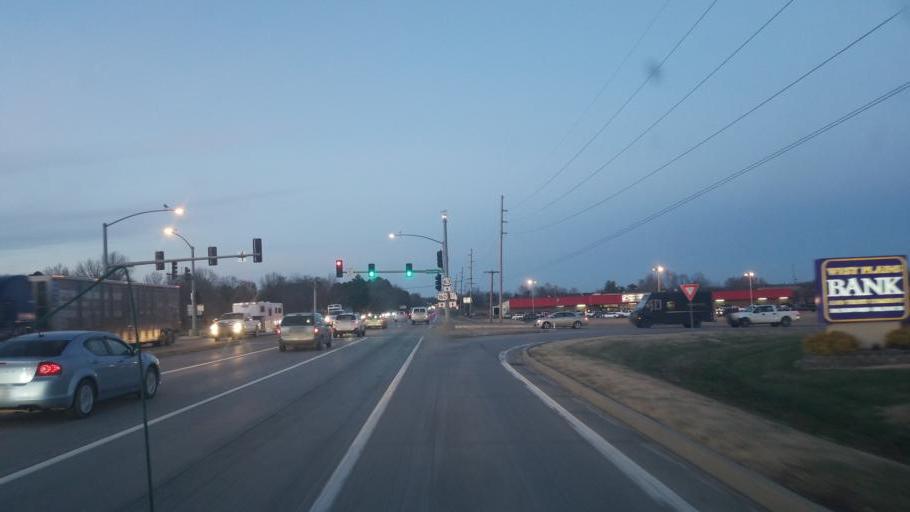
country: US
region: Missouri
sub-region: Howell County
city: West Plains
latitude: 36.7313
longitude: -91.8772
